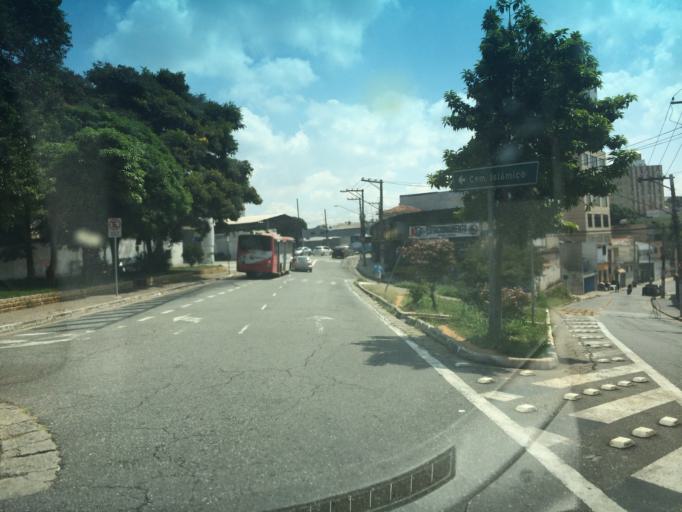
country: BR
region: Sao Paulo
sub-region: Guarulhos
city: Guarulhos
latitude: -23.4537
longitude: -46.5408
